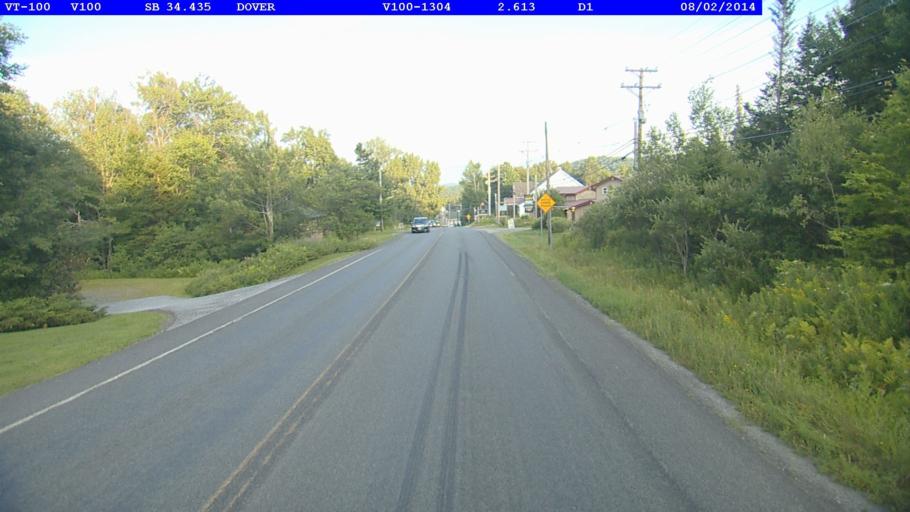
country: US
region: Vermont
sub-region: Windham County
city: Dover
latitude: 42.9509
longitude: -72.8763
